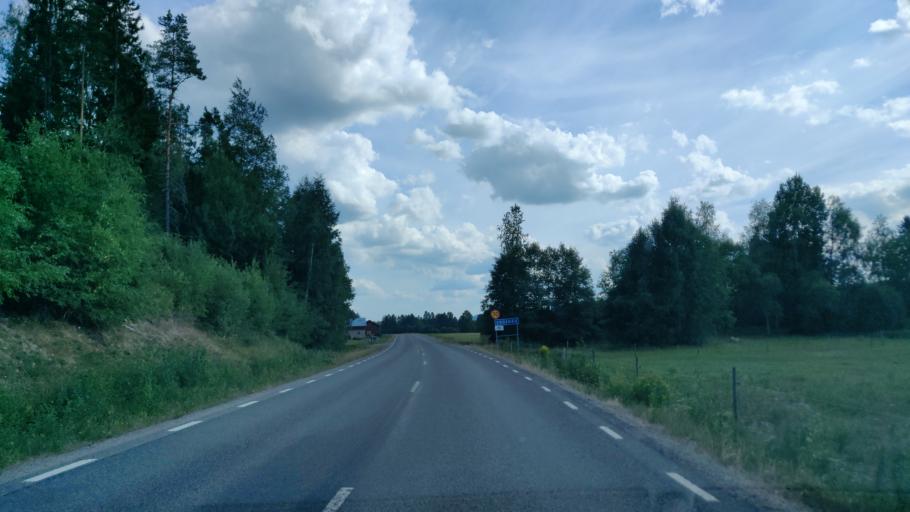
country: SE
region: Vaermland
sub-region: Hagfors Kommun
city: Ekshaerad
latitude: 60.1651
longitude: 13.5316
